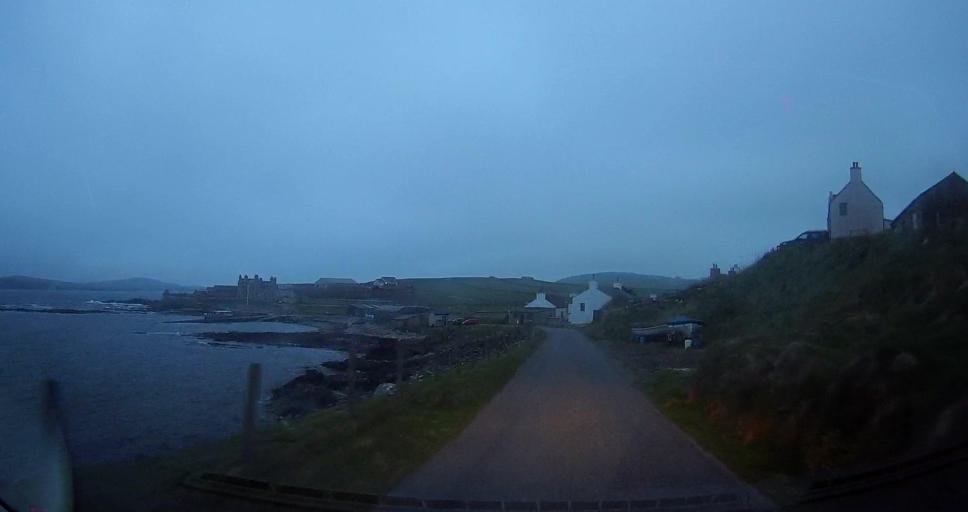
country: GB
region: Scotland
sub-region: Shetland Islands
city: Sandwick
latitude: 60.0080
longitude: -1.2243
